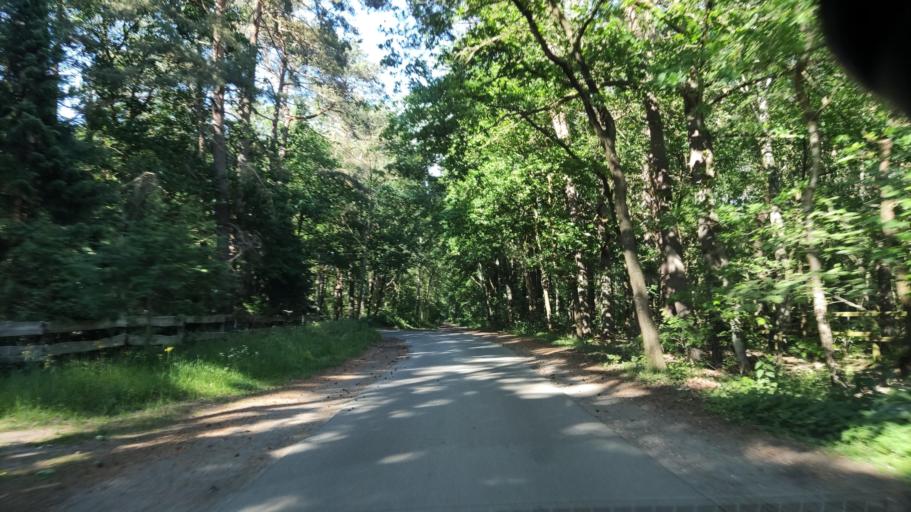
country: DE
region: Lower Saxony
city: Stelle
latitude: 53.3838
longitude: 10.0644
